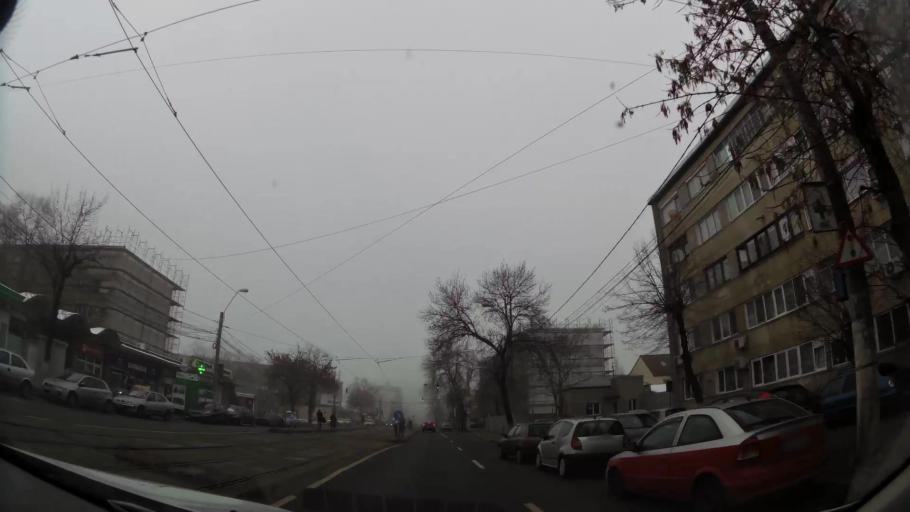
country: RO
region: Ilfov
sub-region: Comuna Chiajna
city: Rosu
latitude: 44.4630
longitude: 26.0423
